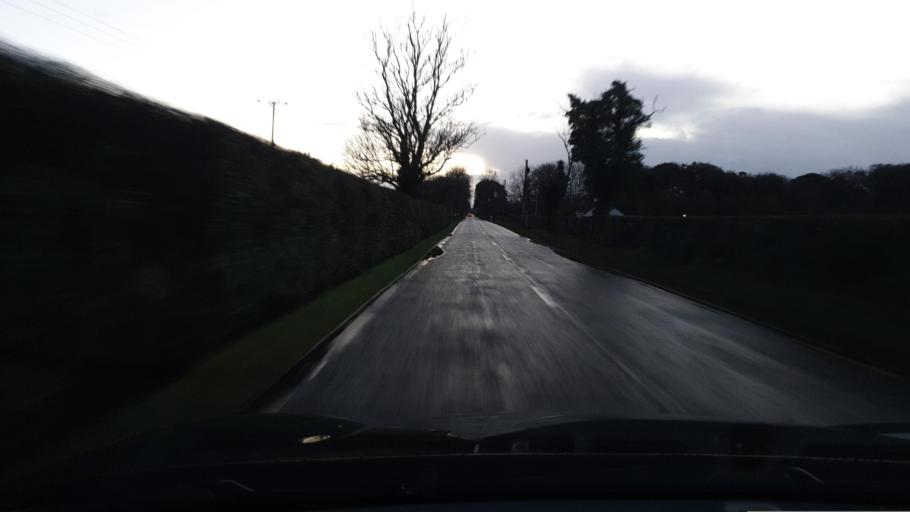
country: IE
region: Leinster
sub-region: Kildare
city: Maynooth
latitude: 53.3627
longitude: -6.6265
